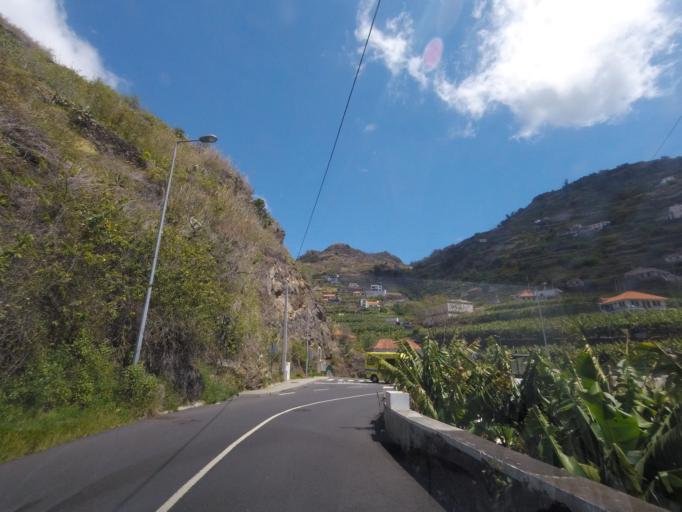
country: PT
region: Madeira
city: Ponta do Sol
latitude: 32.6834
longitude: -17.0751
